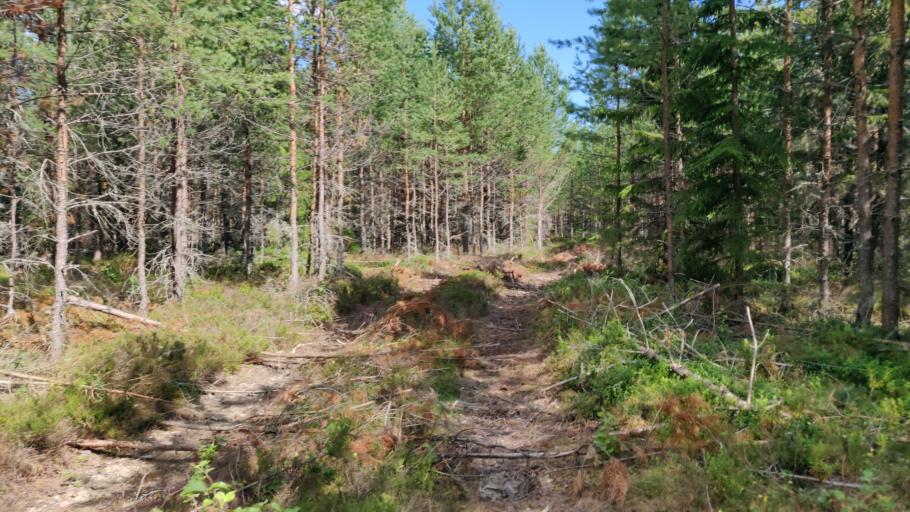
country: SE
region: Vaermland
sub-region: Hagfors Kommun
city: Hagfors
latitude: 60.0285
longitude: 13.5834
